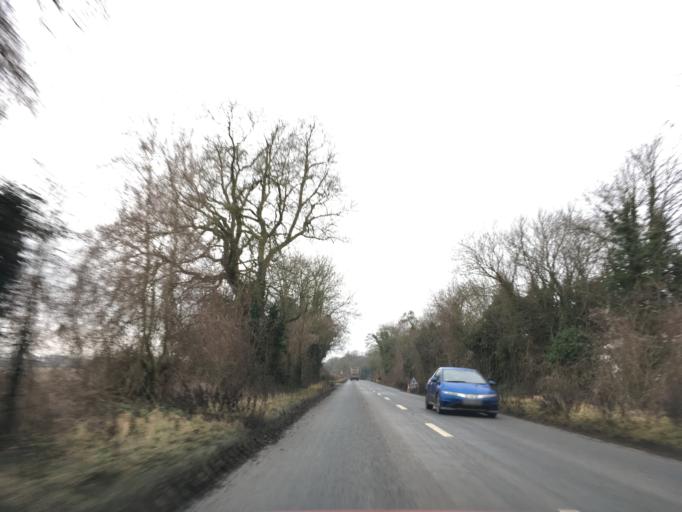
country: GB
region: England
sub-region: Gloucestershire
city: Coates
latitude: 51.6794
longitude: -2.0427
